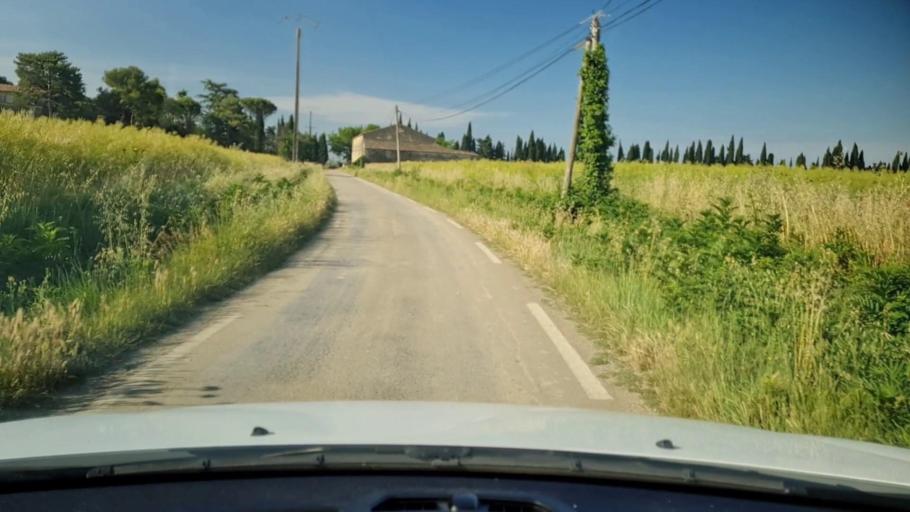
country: FR
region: Languedoc-Roussillon
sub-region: Departement du Gard
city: Aimargues
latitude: 43.6580
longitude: 4.2143
